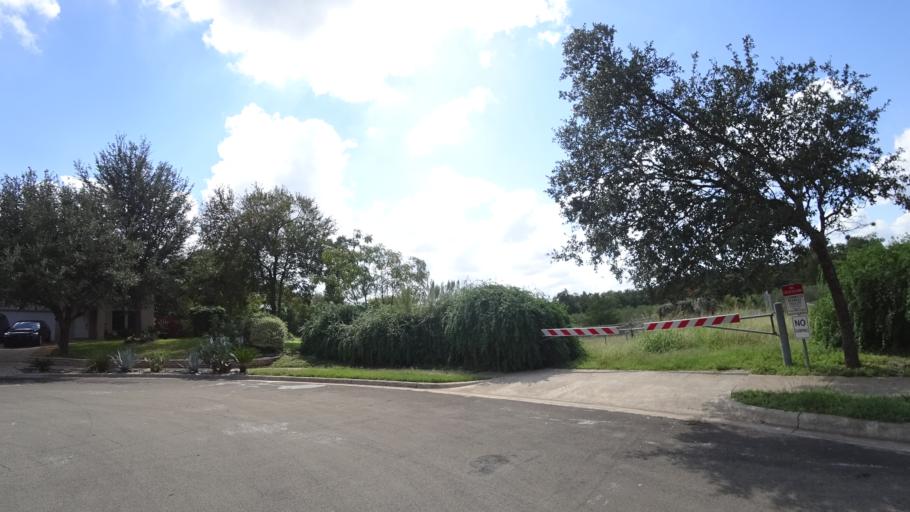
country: US
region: Texas
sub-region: Travis County
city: Manchaca
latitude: 30.1895
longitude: -97.8111
